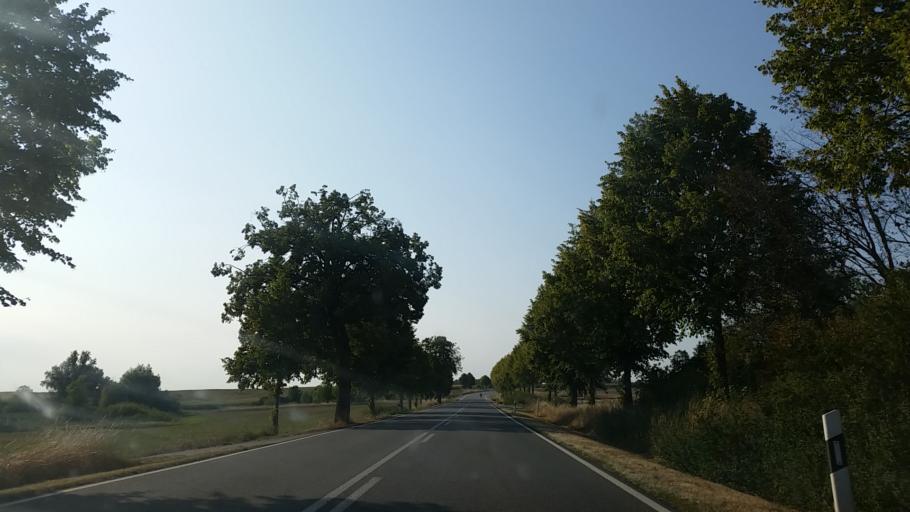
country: DE
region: Brandenburg
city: Zichow
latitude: 53.1766
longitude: 14.0584
